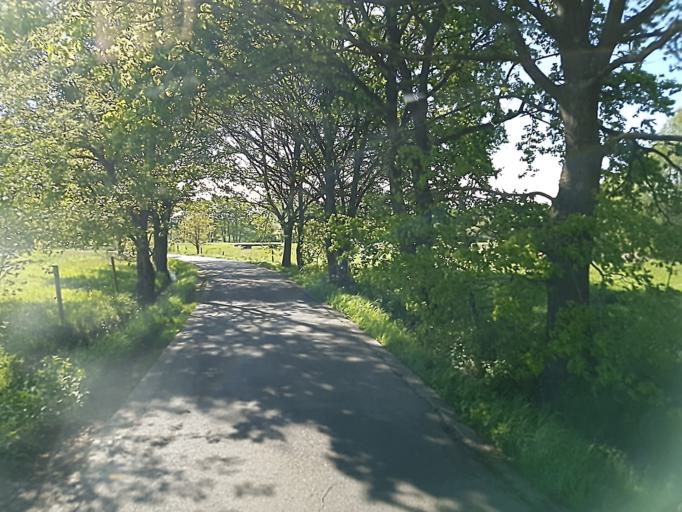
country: BE
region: Flanders
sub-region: Provincie Vlaams-Brabant
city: Boortmeerbeek
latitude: 51.0058
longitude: 4.5731
